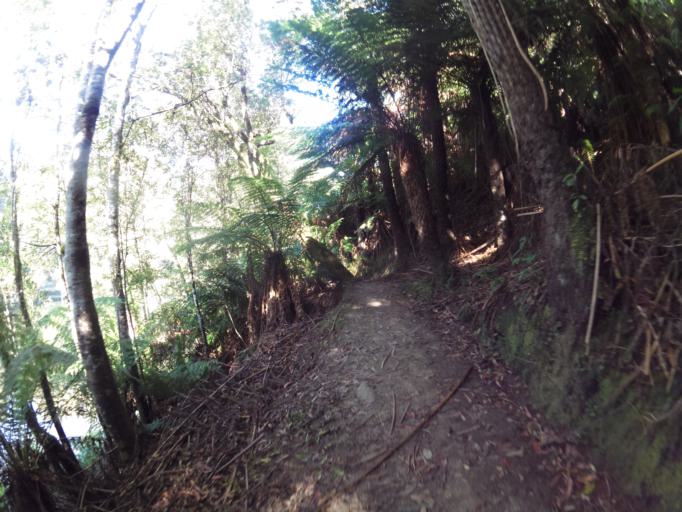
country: AU
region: Victoria
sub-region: Colac-Otway
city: Apollo Bay
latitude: -38.5520
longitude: 143.7574
